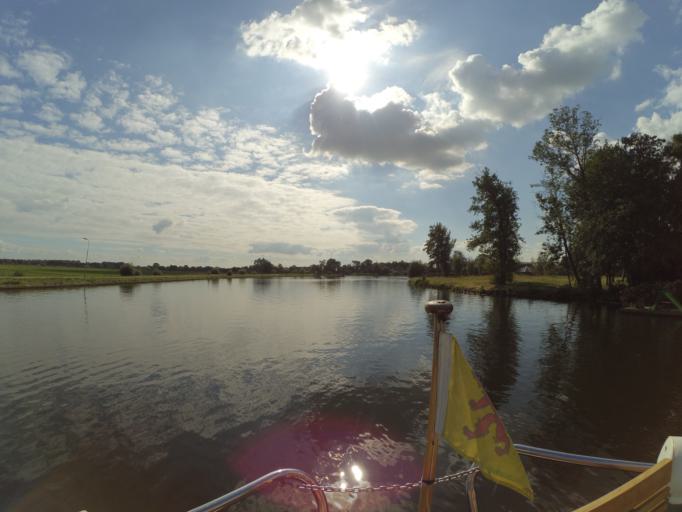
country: NL
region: Utrecht
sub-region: Stichtse Vecht
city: Vreeland
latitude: 52.2606
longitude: 5.0319
